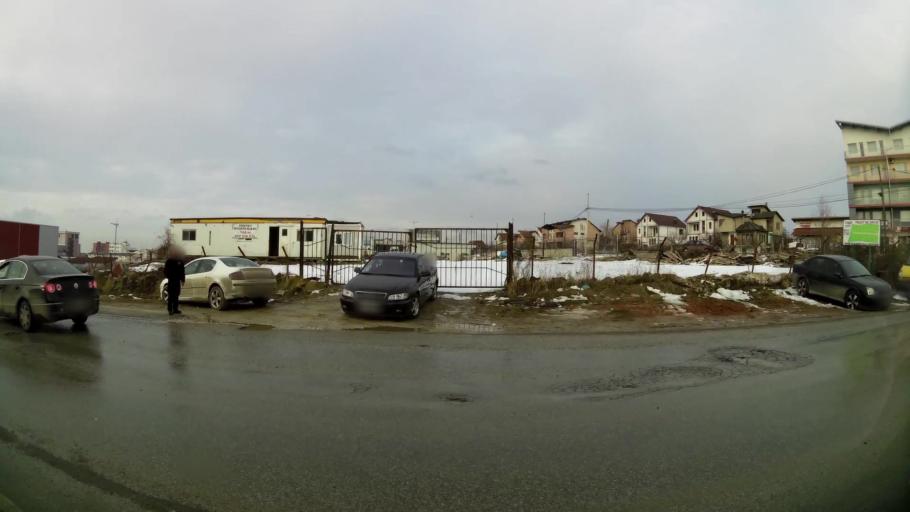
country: XK
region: Pristina
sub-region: Komuna e Prishtines
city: Pristina
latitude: 42.6299
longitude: 21.1569
